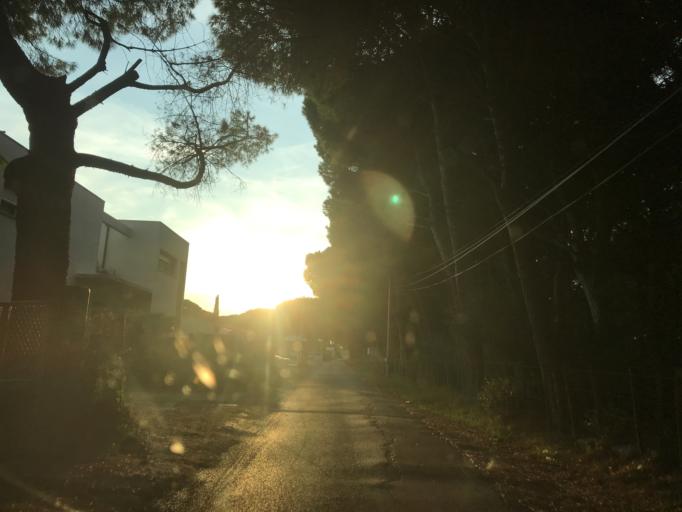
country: FR
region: Languedoc-Roussillon
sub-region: Departement du Gard
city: Aigues-Mortes
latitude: 43.5831
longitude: 4.2032
